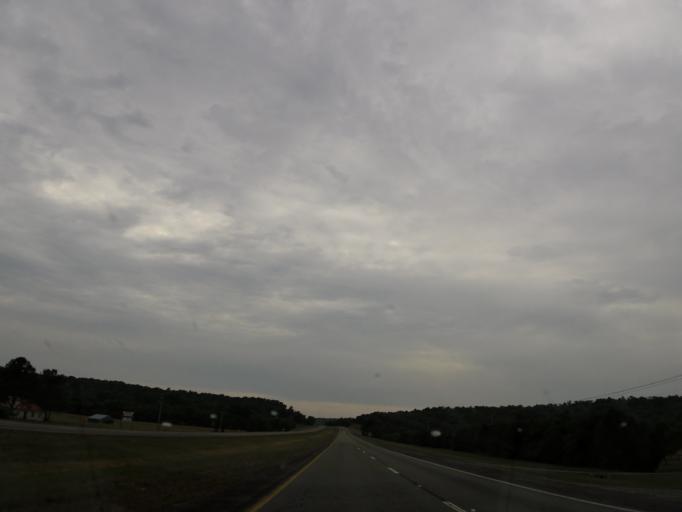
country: US
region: Alabama
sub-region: Madison County
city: New Hope
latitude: 34.6150
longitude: -86.2291
